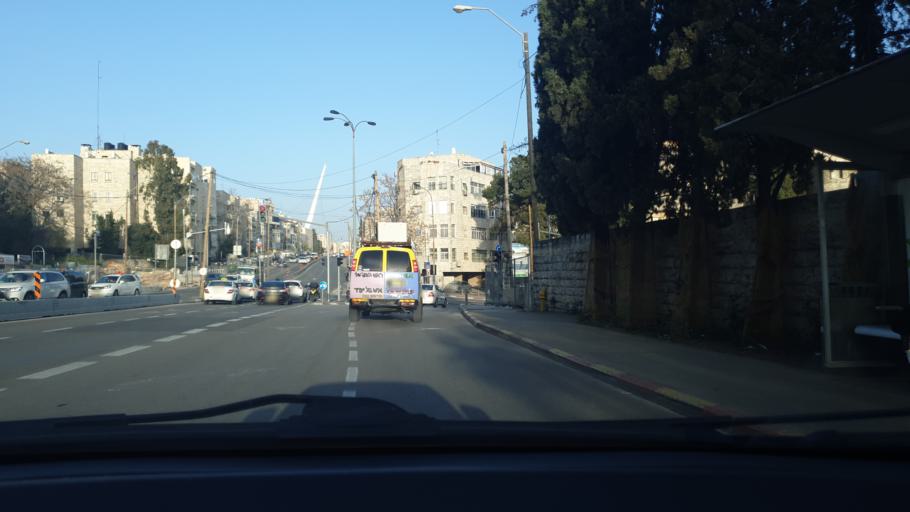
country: IL
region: Jerusalem
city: West Jerusalem
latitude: 31.7874
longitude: 35.1922
